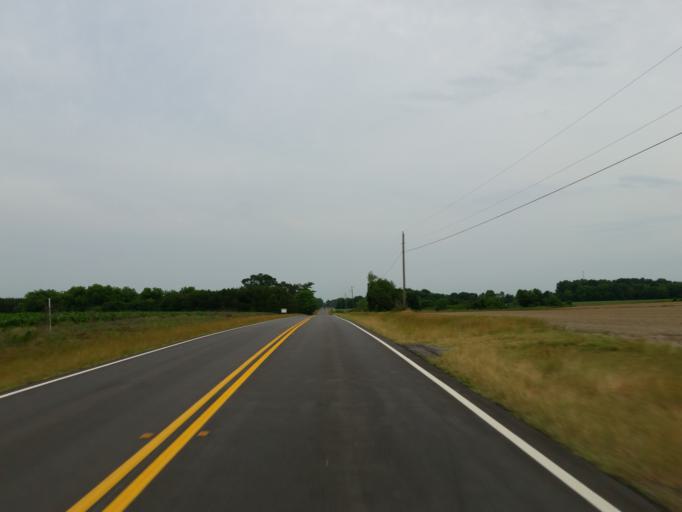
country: US
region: Georgia
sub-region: Dooly County
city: Unadilla
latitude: 32.2948
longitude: -83.7558
